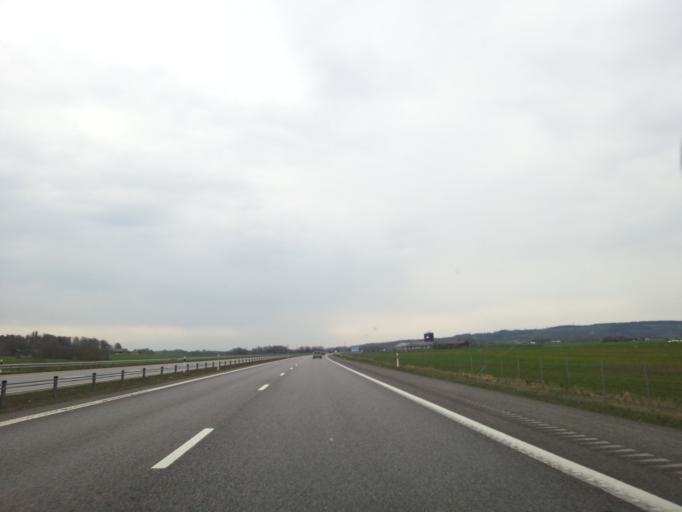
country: SE
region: Halland
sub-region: Halmstads Kommun
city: Getinge
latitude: 56.7904
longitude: 12.7898
